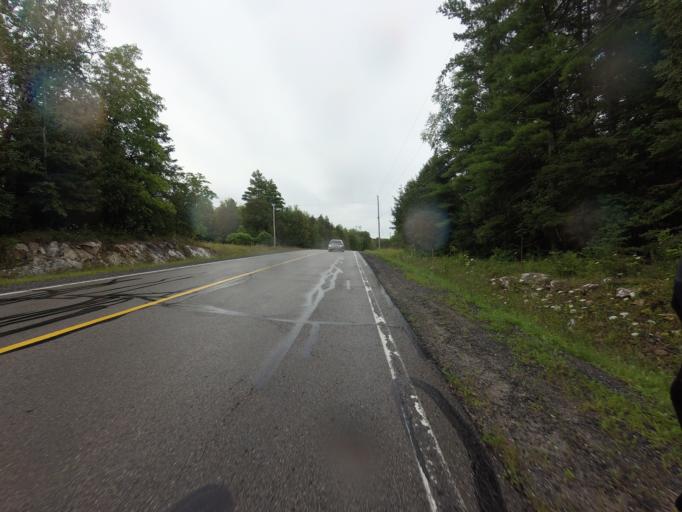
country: CA
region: Ontario
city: Perth
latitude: 44.9996
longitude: -76.3779
